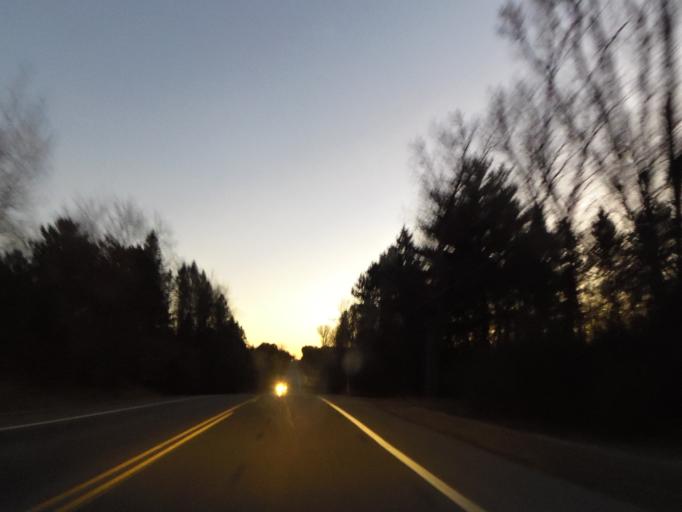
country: US
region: Minnesota
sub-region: Washington County
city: Stillwater
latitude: 45.0984
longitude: -92.8334
